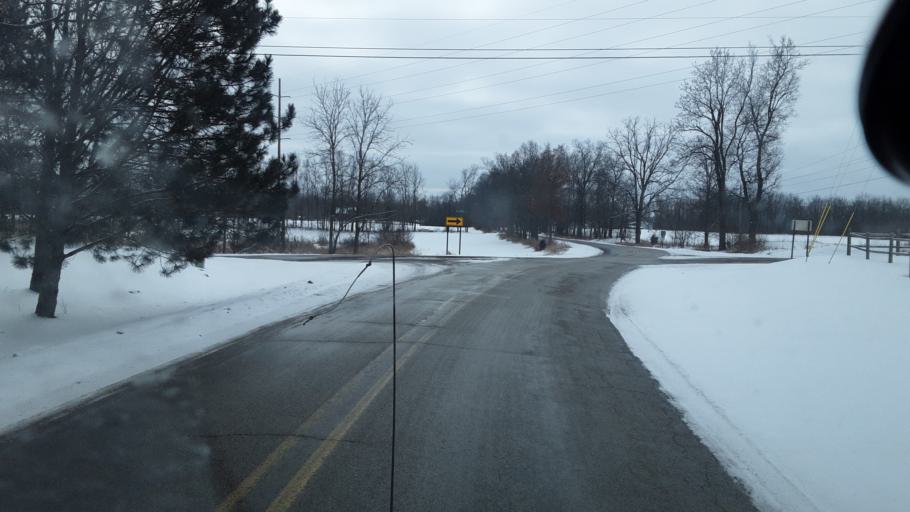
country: US
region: Michigan
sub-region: Ingham County
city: Leslie
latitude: 42.5099
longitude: -84.3888
